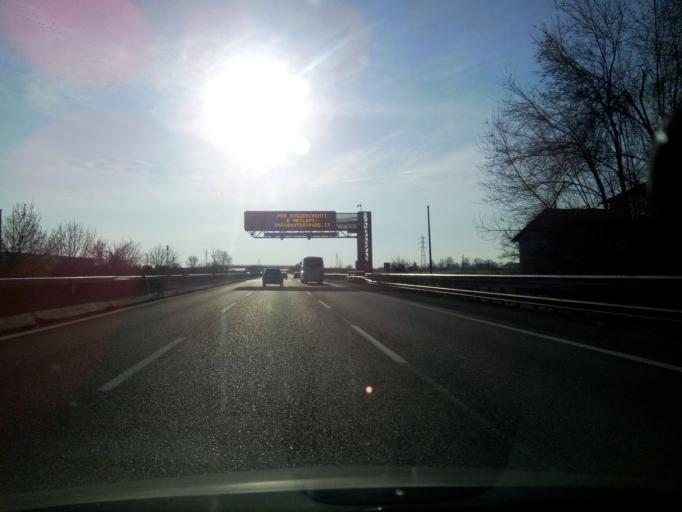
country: IT
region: Emilia-Romagna
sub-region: Provincia di Parma
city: Fontanellato
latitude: 44.8708
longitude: 10.2036
